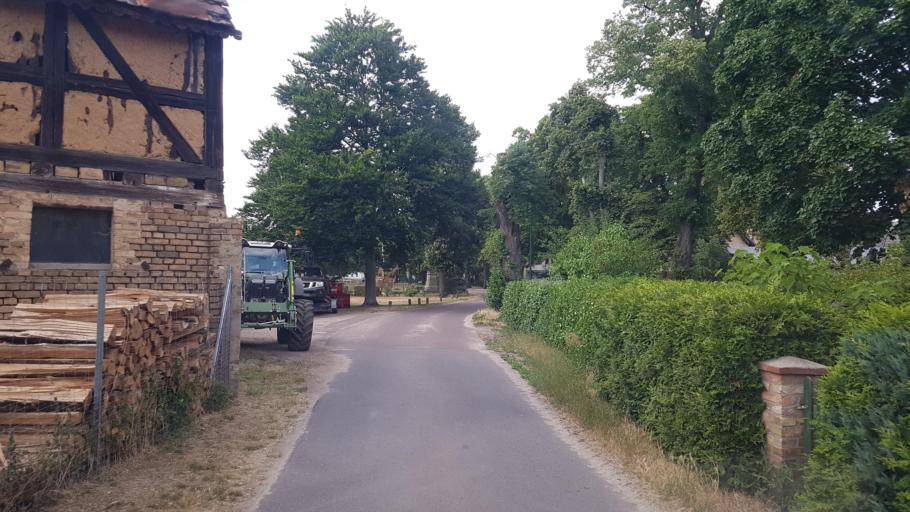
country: DE
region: Brandenburg
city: Golzow
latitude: 52.2387
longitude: 12.5832
